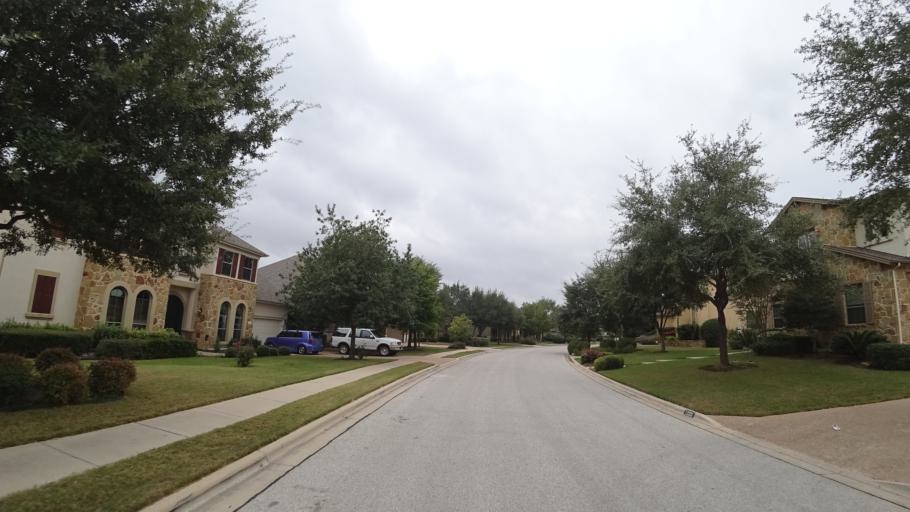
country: US
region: Texas
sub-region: Travis County
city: Hudson Bend
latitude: 30.3580
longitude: -97.9000
